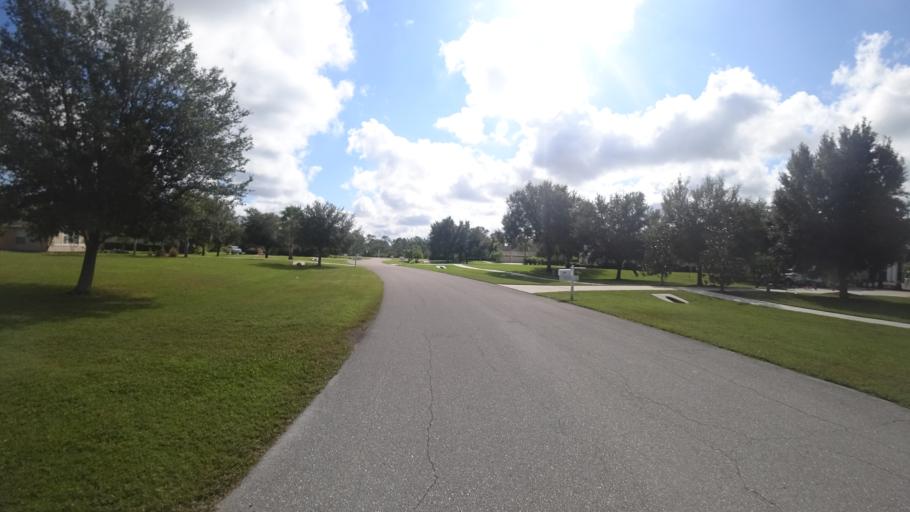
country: US
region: Florida
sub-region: Sarasota County
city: Fruitville
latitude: 27.3932
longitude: -82.3056
